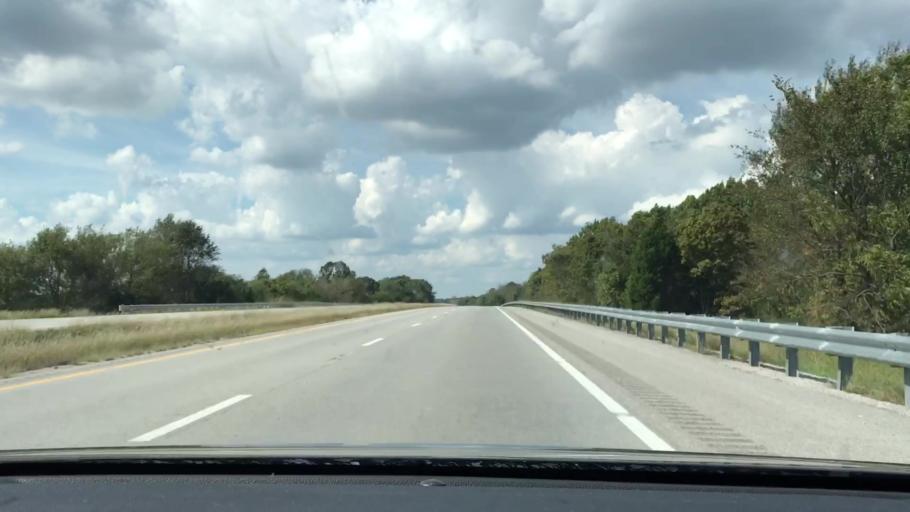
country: US
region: Kentucky
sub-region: Barren County
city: Glasgow
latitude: 37.0027
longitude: -86.0012
